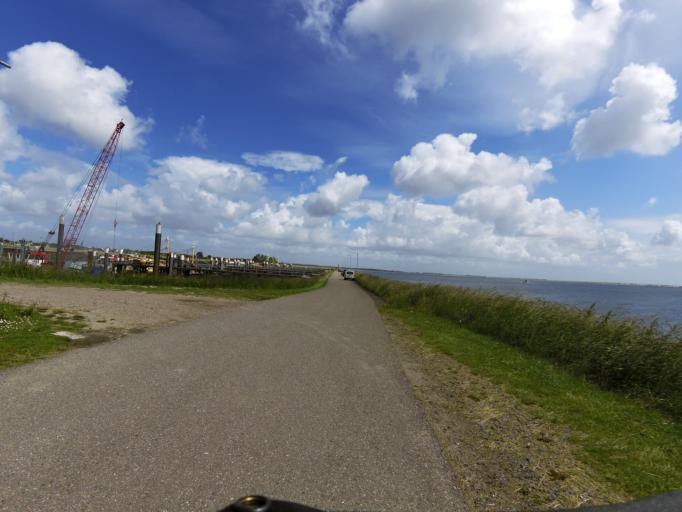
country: NL
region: Zeeland
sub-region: Schouwen-Duiveland
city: Bruinisse
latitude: 51.6507
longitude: 4.0989
